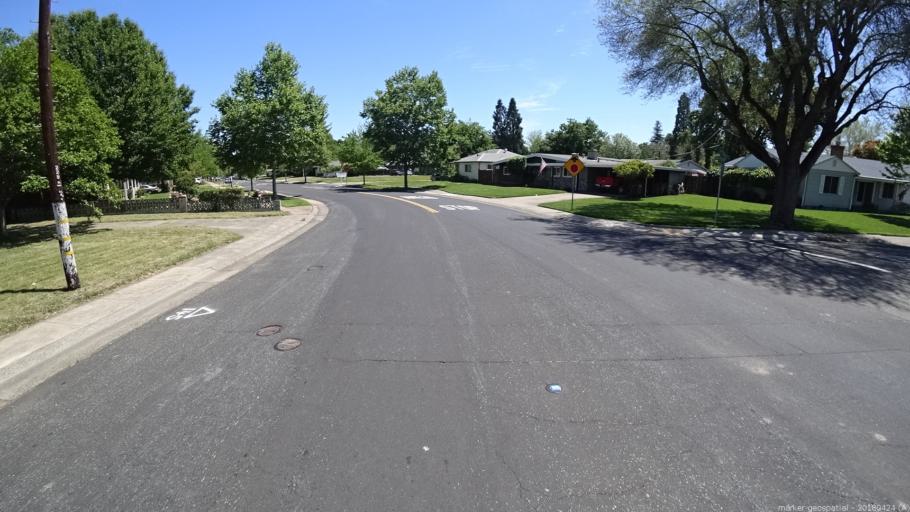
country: US
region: California
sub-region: Yolo County
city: West Sacramento
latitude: 38.5709
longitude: -121.5292
